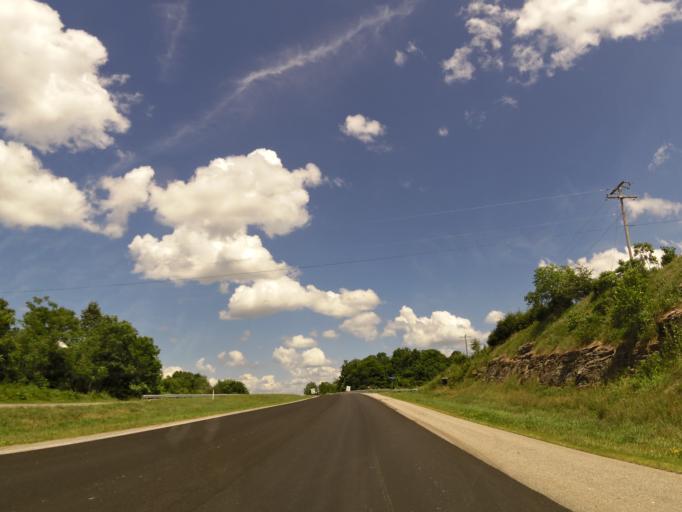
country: US
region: Virginia
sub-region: Lee County
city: Jonesville
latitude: 36.6967
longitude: -83.2668
